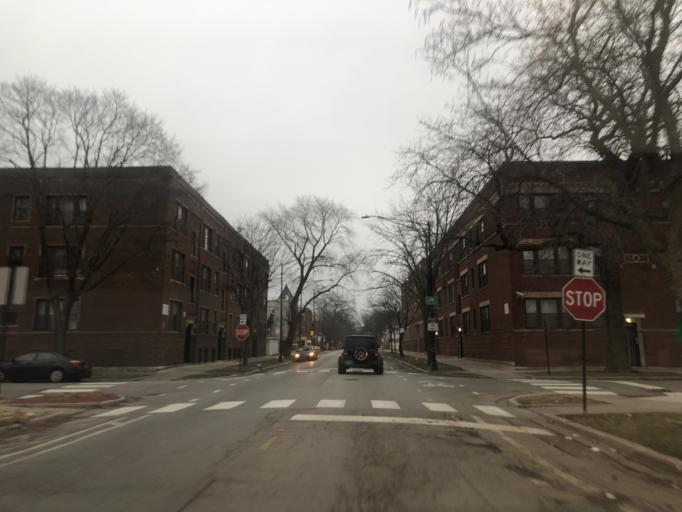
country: US
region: Illinois
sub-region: Cook County
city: Chicago
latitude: 41.7751
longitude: -87.6013
